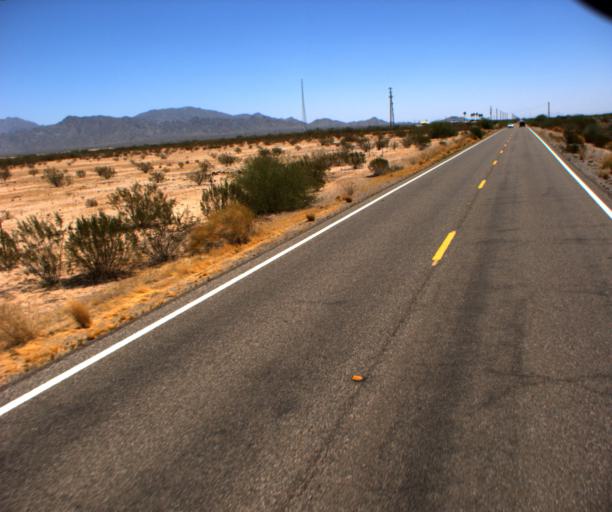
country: US
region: Arizona
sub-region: Pinal County
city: Maricopa
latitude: 33.0534
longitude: -112.2799
